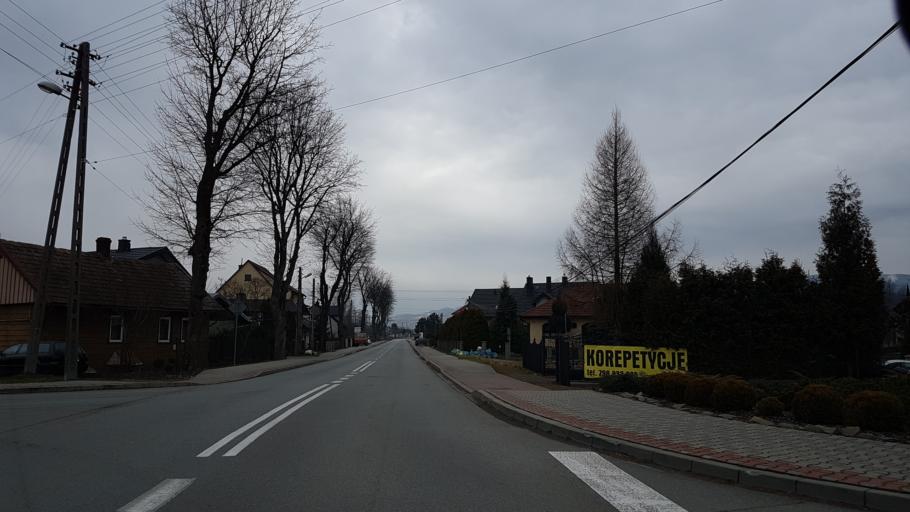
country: PL
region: Lesser Poland Voivodeship
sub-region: Powiat nowosadecki
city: Stary Sacz
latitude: 49.5421
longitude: 20.6445
